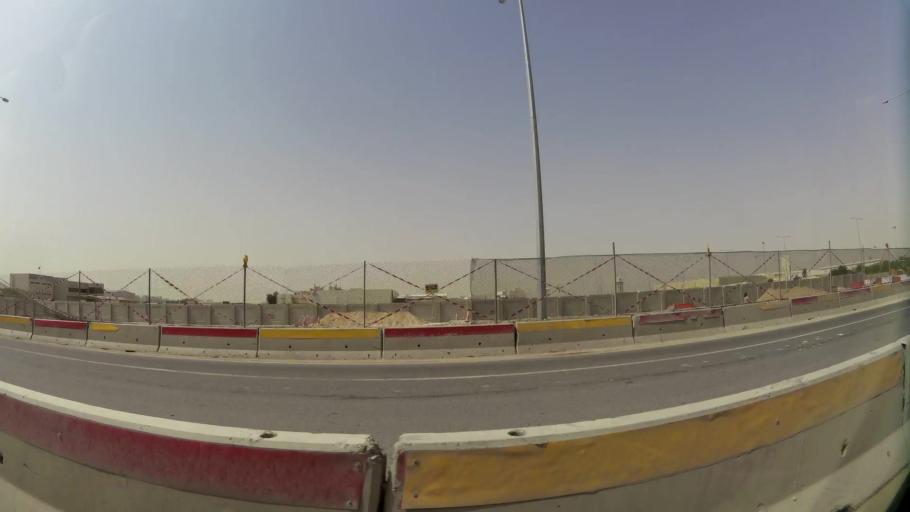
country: QA
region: Baladiyat ar Rayyan
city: Ar Rayyan
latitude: 25.2117
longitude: 51.4203
